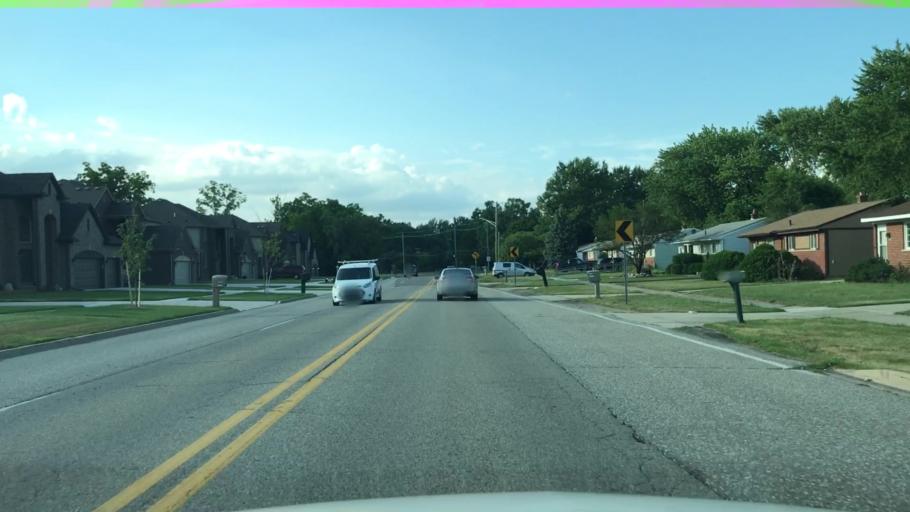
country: US
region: Michigan
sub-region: Macomb County
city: Sterling Heights
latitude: 42.5977
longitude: -83.0048
